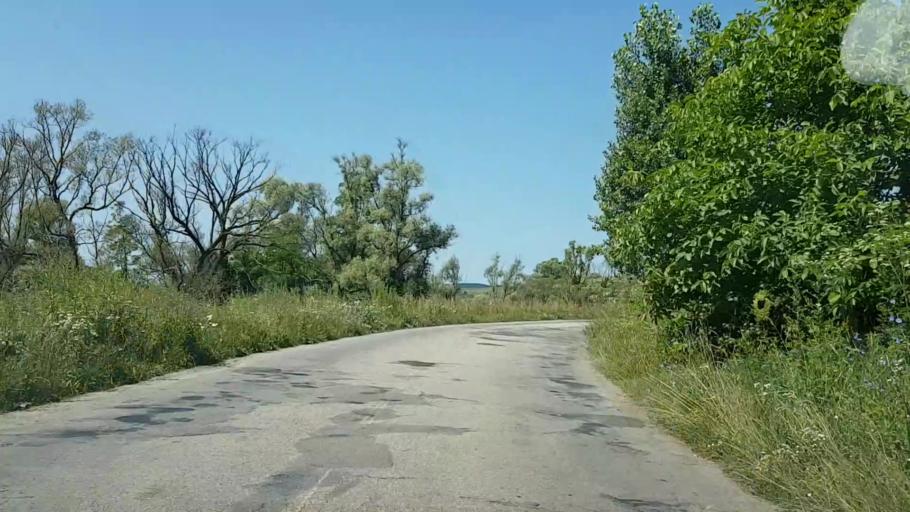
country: RO
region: Sibiu
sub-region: Comuna Iacobeni
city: Iacobeni
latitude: 46.0418
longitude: 24.7407
